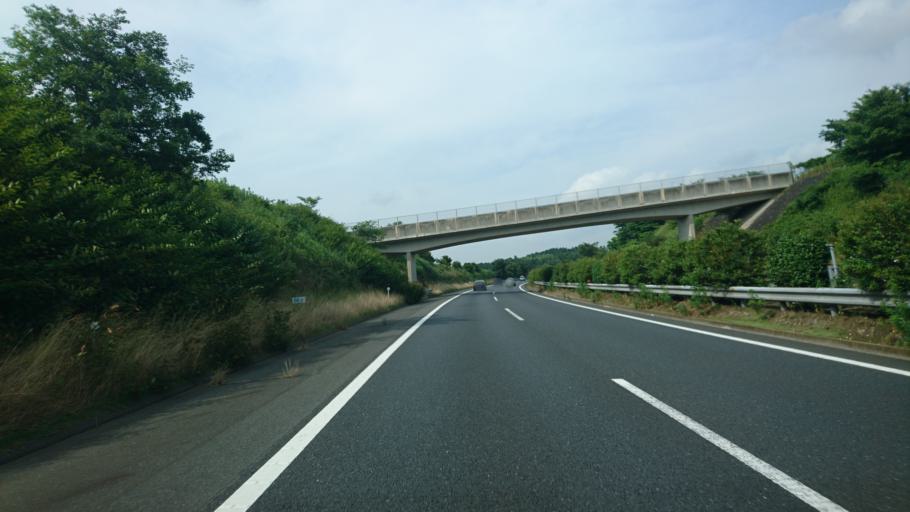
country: JP
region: Chiba
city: Kisarazu
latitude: 35.4201
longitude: 140.0130
